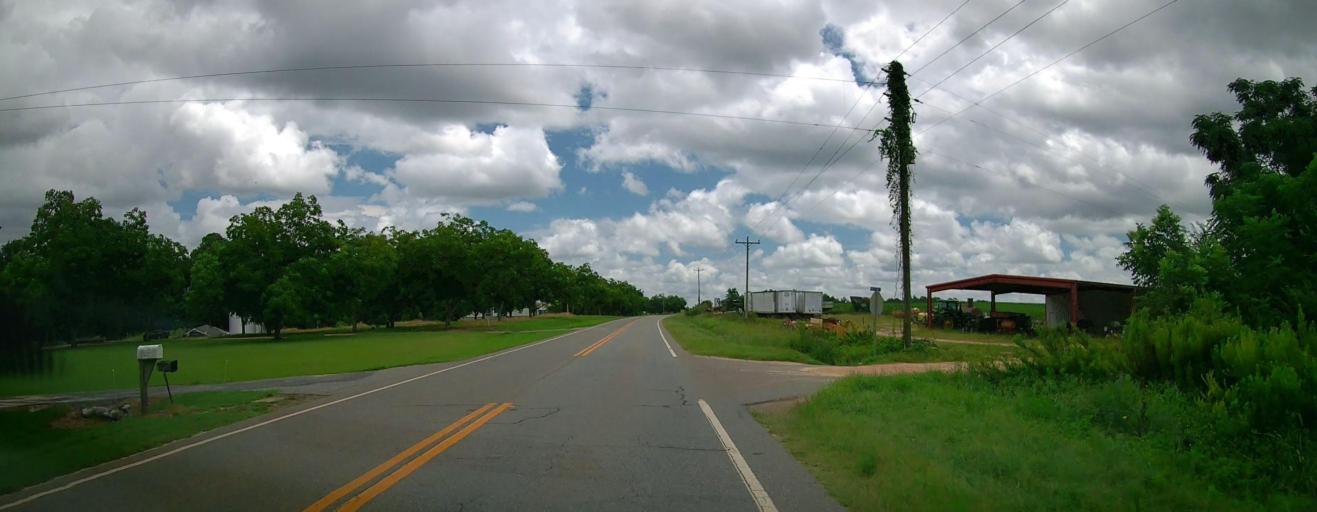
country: US
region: Georgia
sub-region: Wilcox County
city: Rochelle
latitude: 31.9954
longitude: -83.5545
